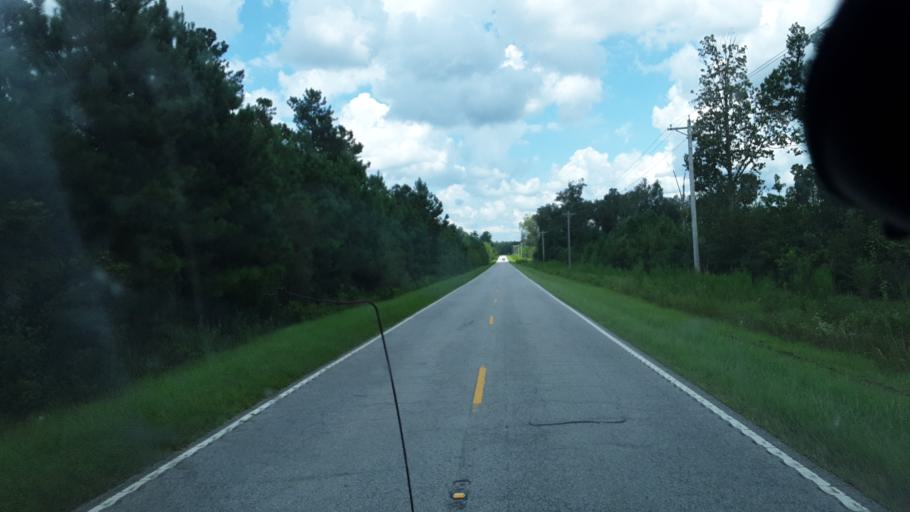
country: US
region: South Carolina
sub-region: Florence County
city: Johnsonville
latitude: 33.6405
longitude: -79.4235
